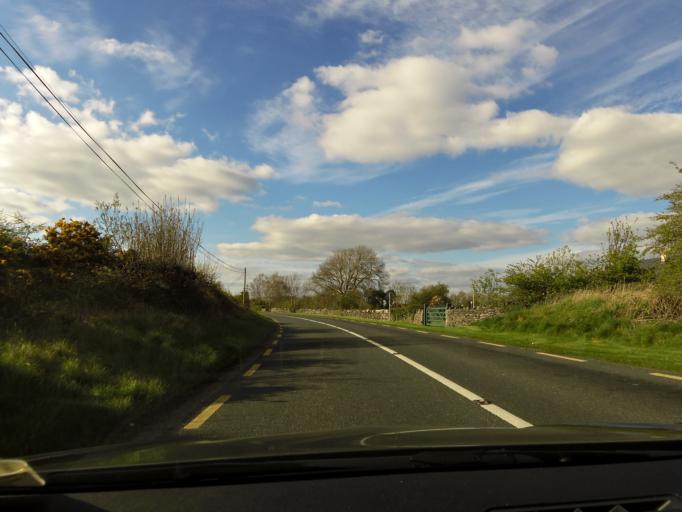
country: IE
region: Connaught
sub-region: County Galway
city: Portumna
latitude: 53.1129
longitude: -8.2371
